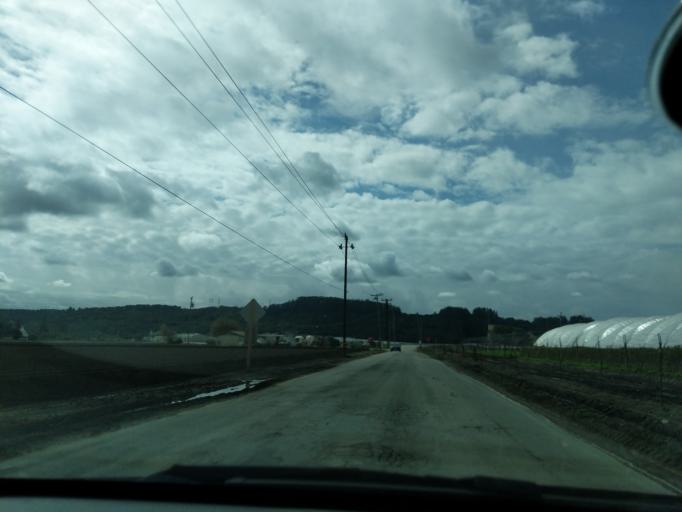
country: US
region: California
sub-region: San Benito County
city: Aromas
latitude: 36.8983
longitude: -121.6761
